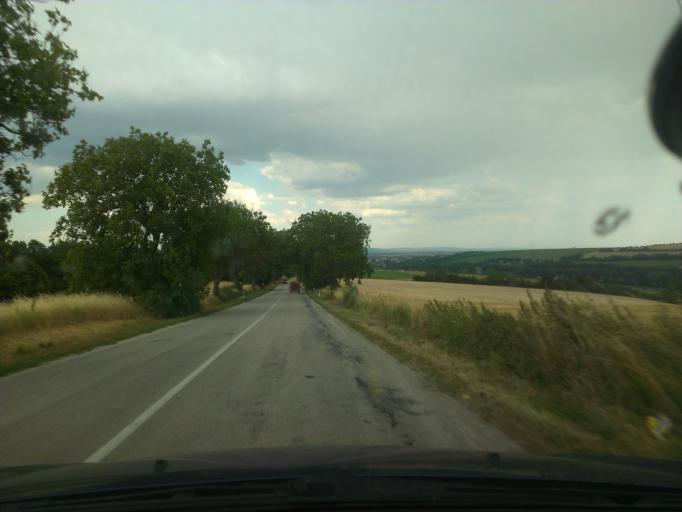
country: SK
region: Trnavsky
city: Vrbove
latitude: 48.6514
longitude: 17.7061
